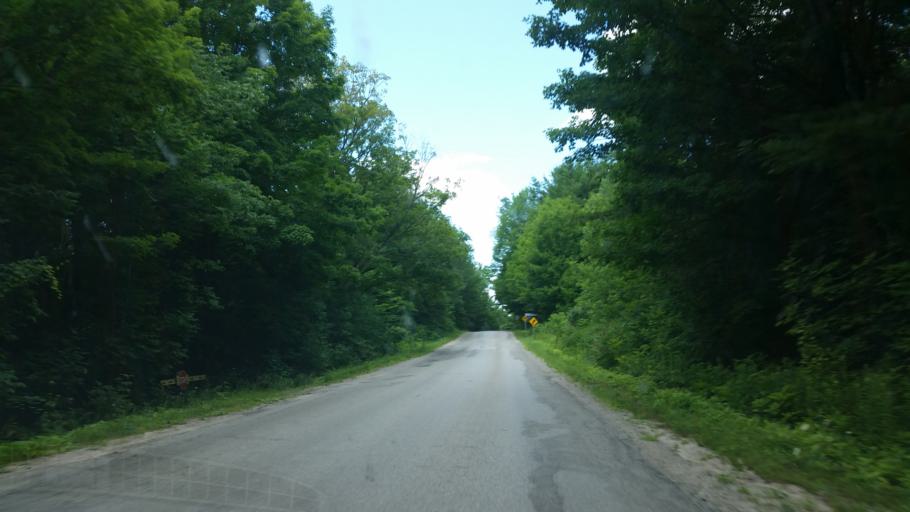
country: CA
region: Ontario
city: Barrie
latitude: 44.4474
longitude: -79.7101
